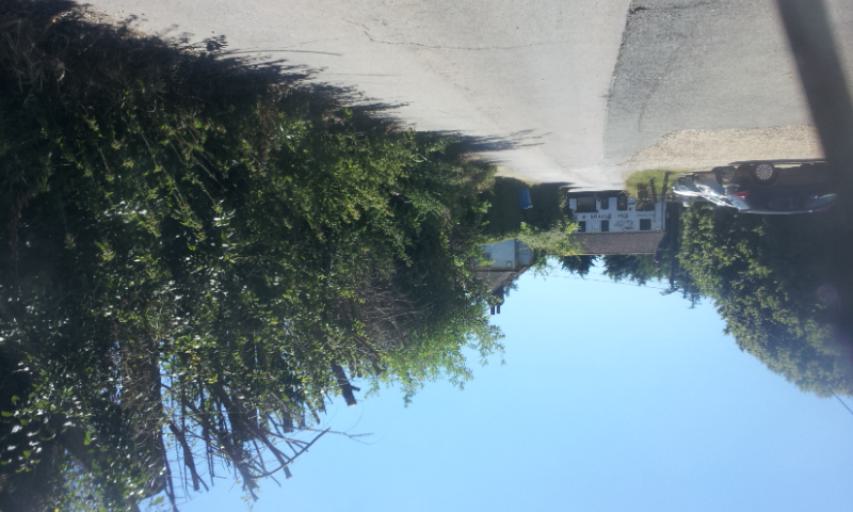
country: GB
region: England
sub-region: Kent
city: Newington
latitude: 51.3281
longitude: 0.6829
